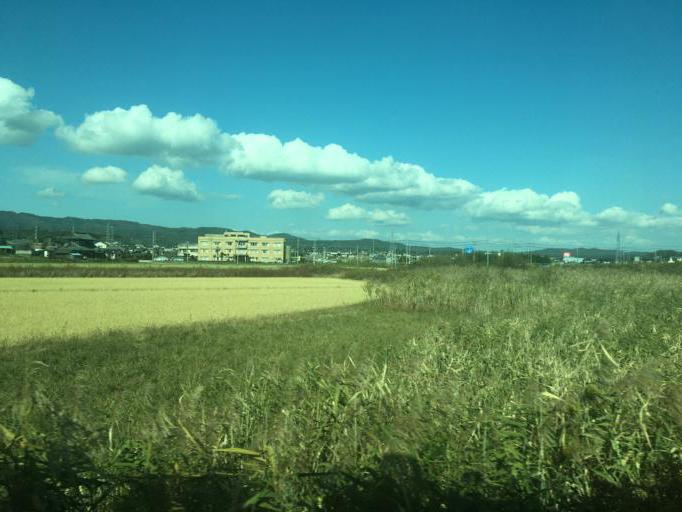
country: JP
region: Ibaraki
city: Kasama
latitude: 36.3754
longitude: 140.2383
